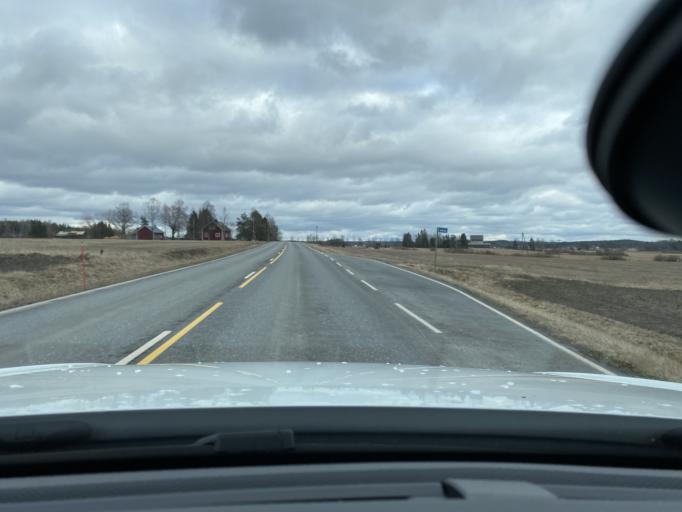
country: FI
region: Pirkanmaa
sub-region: Lounais-Pirkanmaa
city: Punkalaidun
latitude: 61.1051
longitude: 23.1435
